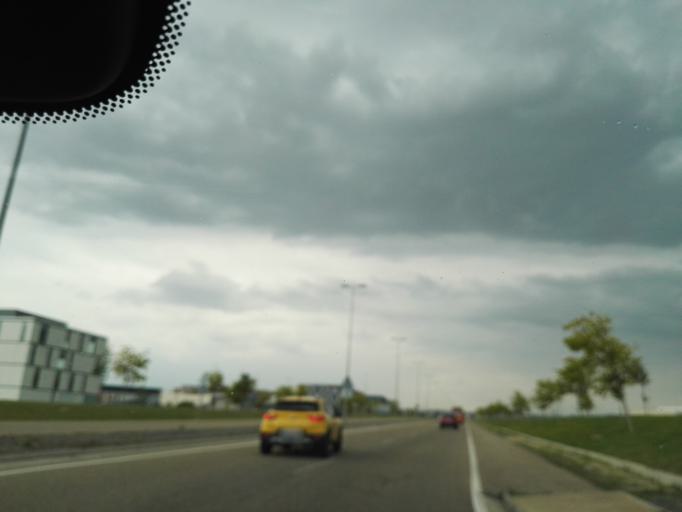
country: ES
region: Aragon
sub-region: Provincia de Zaragoza
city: Montecanal
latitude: 41.6458
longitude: -0.9959
